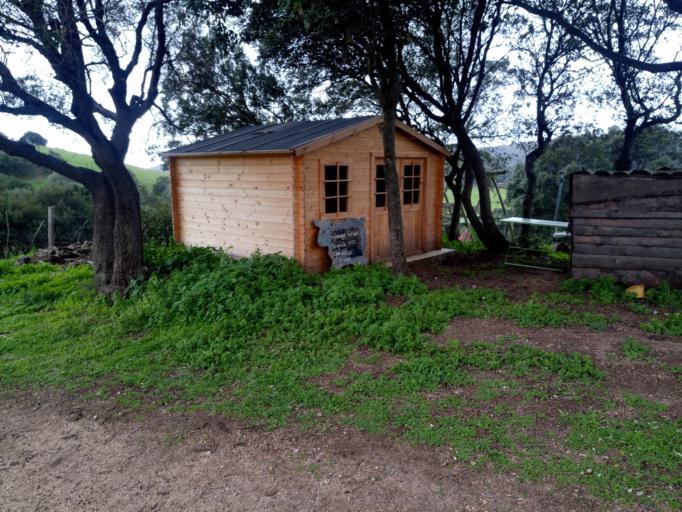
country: FR
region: Corsica
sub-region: Departement de la Corse-du-Sud
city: Sartene
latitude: 41.5239
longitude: 8.9512
